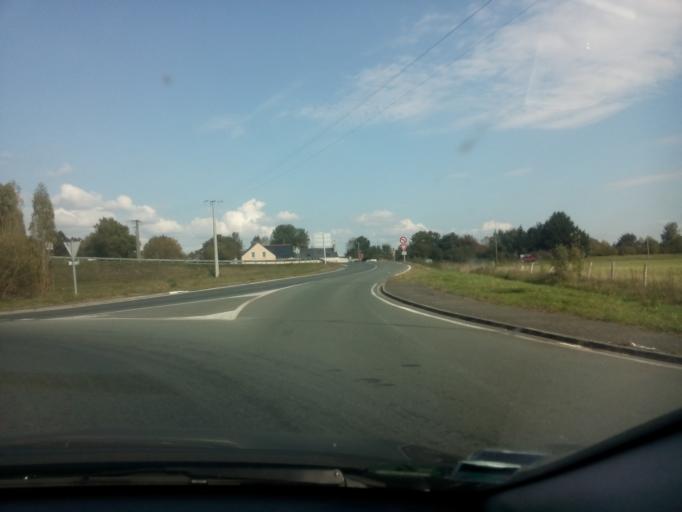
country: FR
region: Pays de la Loire
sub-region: Departement de Maine-et-Loire
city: Ecouflant
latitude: 47.5237
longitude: -0.5015
